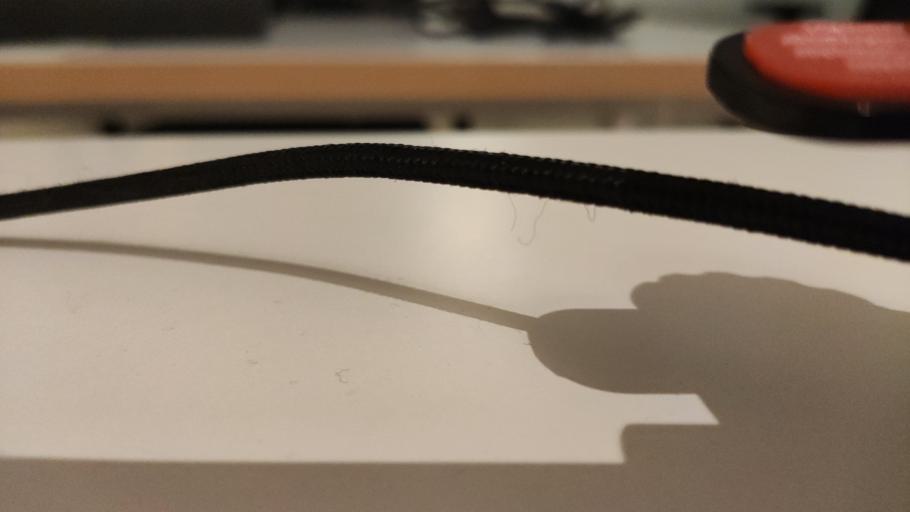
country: RU
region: Moskovskaya
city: Shaburnovo
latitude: 56.4274
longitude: 37.9535
